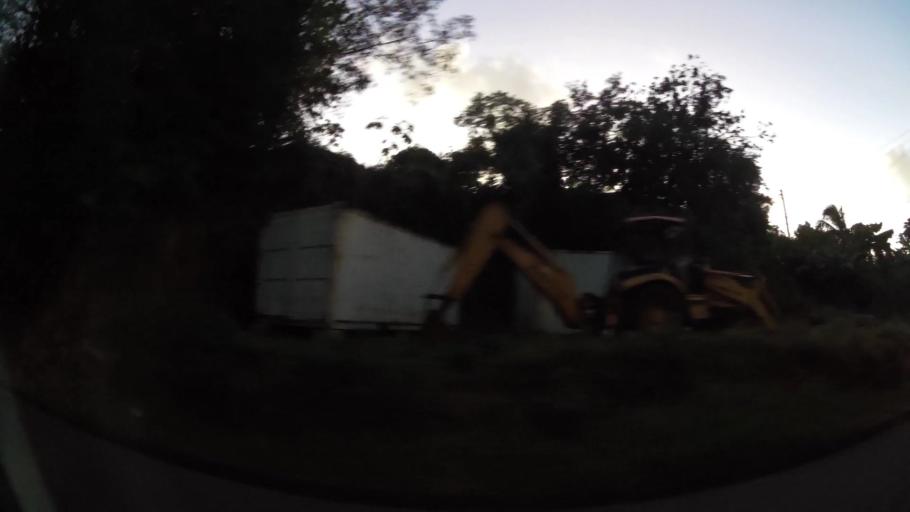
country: LC
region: Castries Quarter
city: Bisee
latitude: 14.0365
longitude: -60.9506
